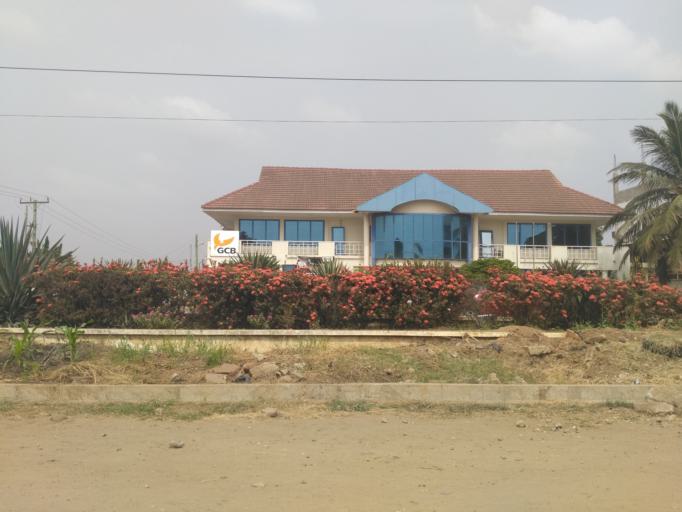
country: GH
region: Greater Accra
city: Nungua
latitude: 5.5967
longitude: -0.0840
